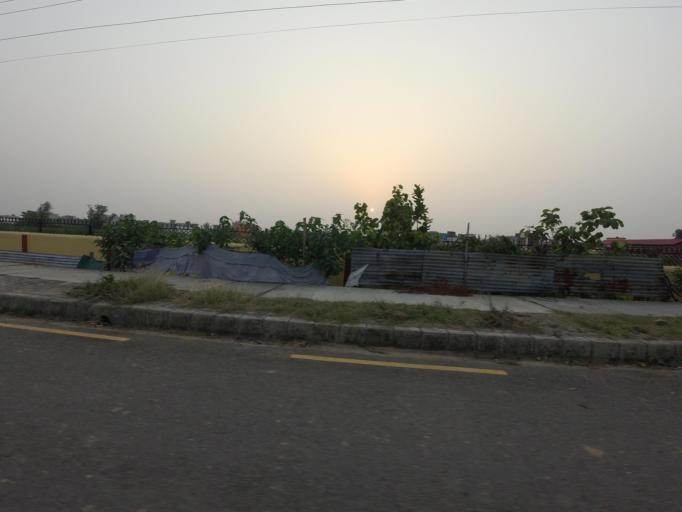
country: NP
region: Western Region
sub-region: Lumbini Zone
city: Bhairahawa
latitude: 27.4997
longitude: 83.4627
